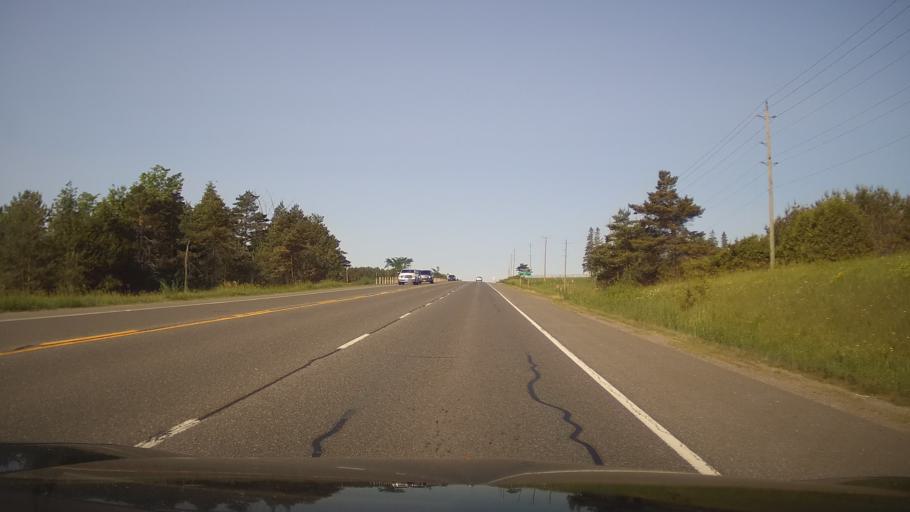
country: CA
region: Ontario
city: Peterborough
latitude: 44.3405
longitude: -78.0943
